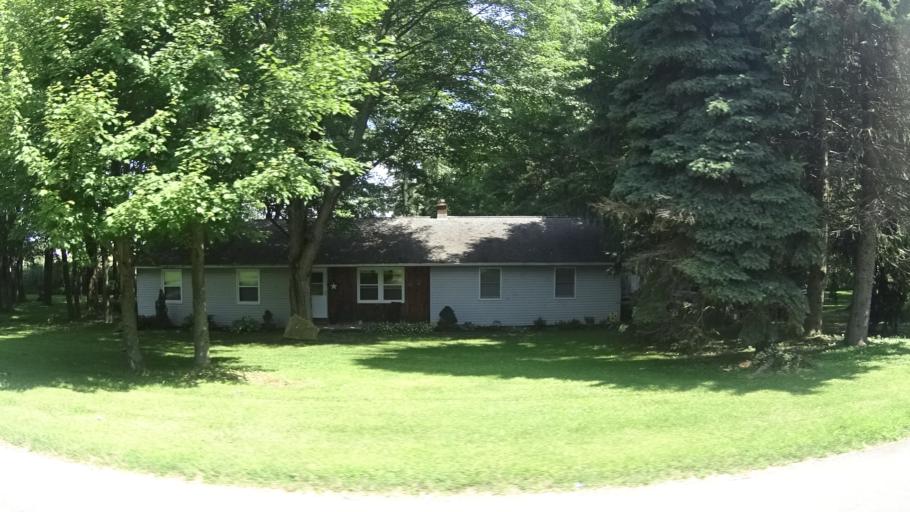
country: US
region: Ohio
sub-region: Lorain County
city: Vermilion
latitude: 41.3537
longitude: -82.4368
